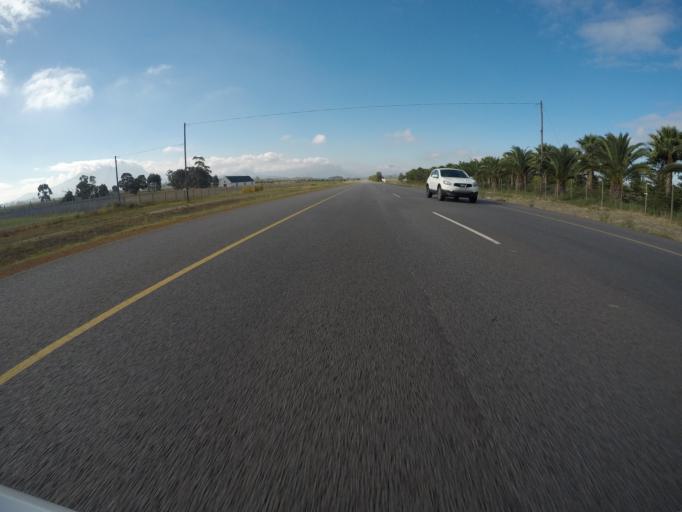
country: ZA
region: Western Cape
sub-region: City of Cape Town
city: Kraaifontein
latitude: -33.8406
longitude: 18.8000
